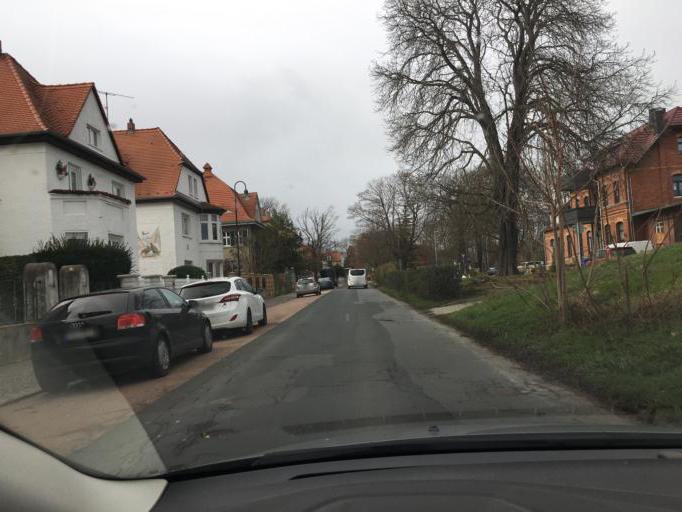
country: DE
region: Saxony-Anhalt
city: Bad Lauchstadt
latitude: 51.3887
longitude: 11.8730
